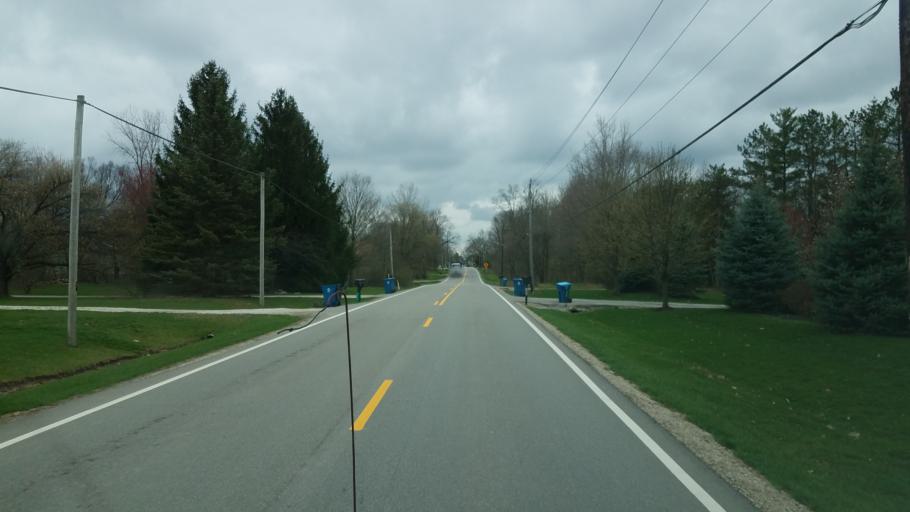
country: US
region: Ohio
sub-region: Delaware County
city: Powell
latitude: 40.2203
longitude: -83.1327
